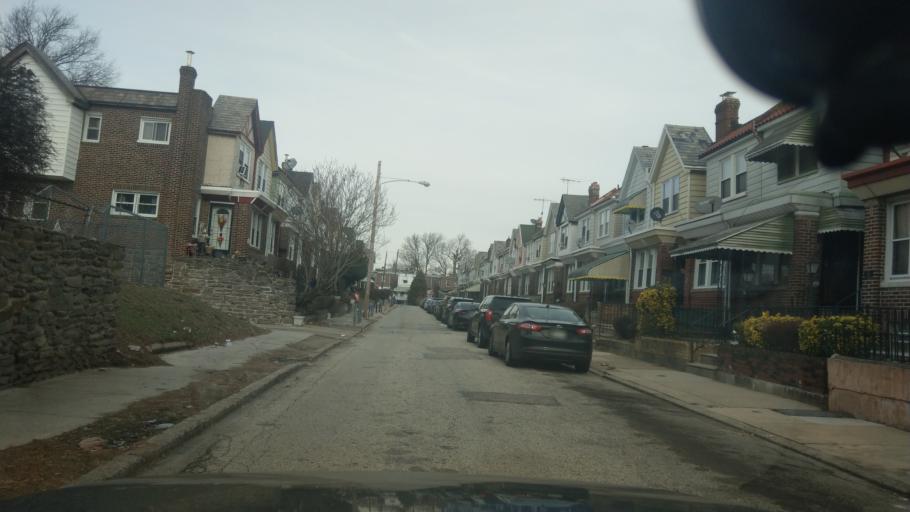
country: US
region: Pennsylvania
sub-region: Montgomery County
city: Wyncote
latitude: 40.0484
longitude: -75.1484
